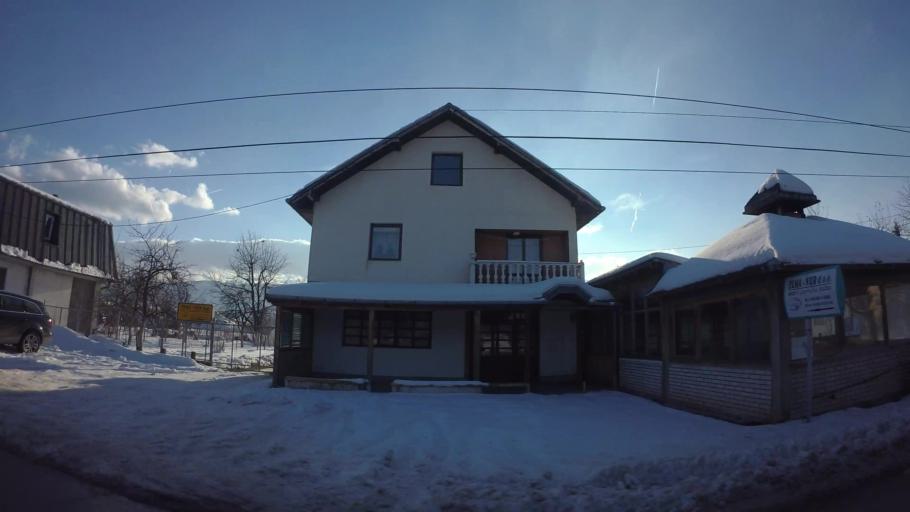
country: BA
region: Federation of Bosnia and Herzegovina
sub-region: Kanton Sarajevo
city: Sarajevo
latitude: 43.8153
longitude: 18.3384
